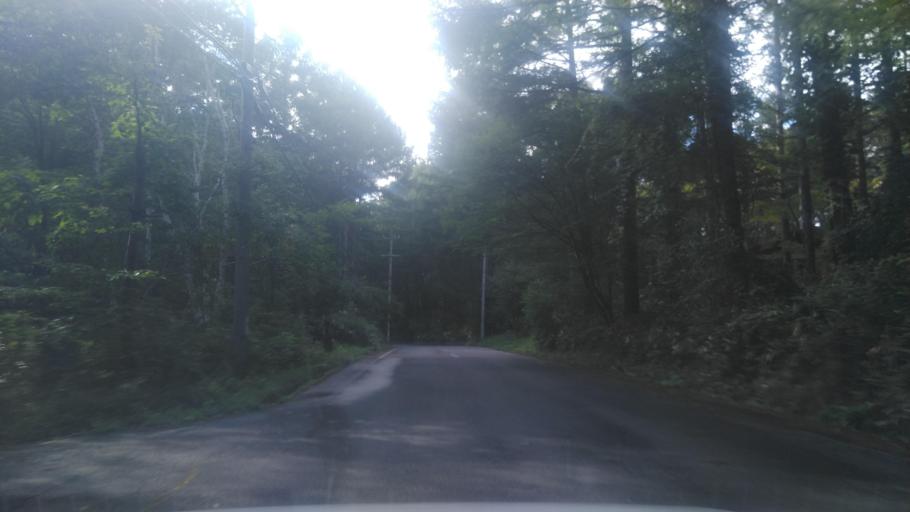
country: JP
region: Nagano
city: Ueda
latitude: 36.5149
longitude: 138.3597
